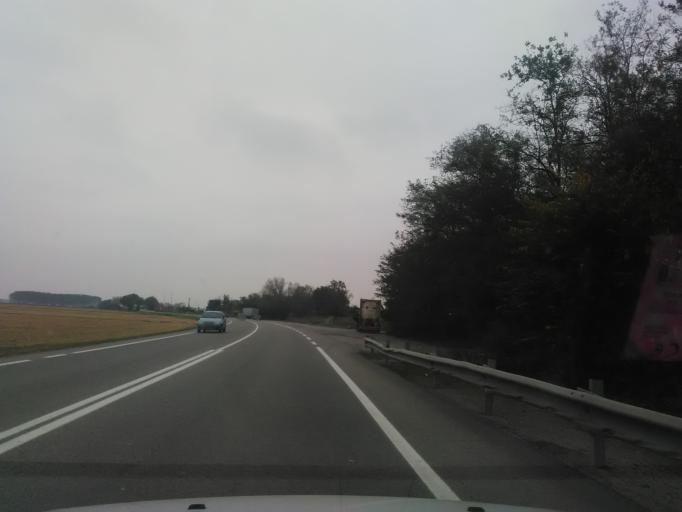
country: IT
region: Piedmont
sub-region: Provincia di Vercelli
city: Vercelli
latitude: 45.3066
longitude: 8.4037
